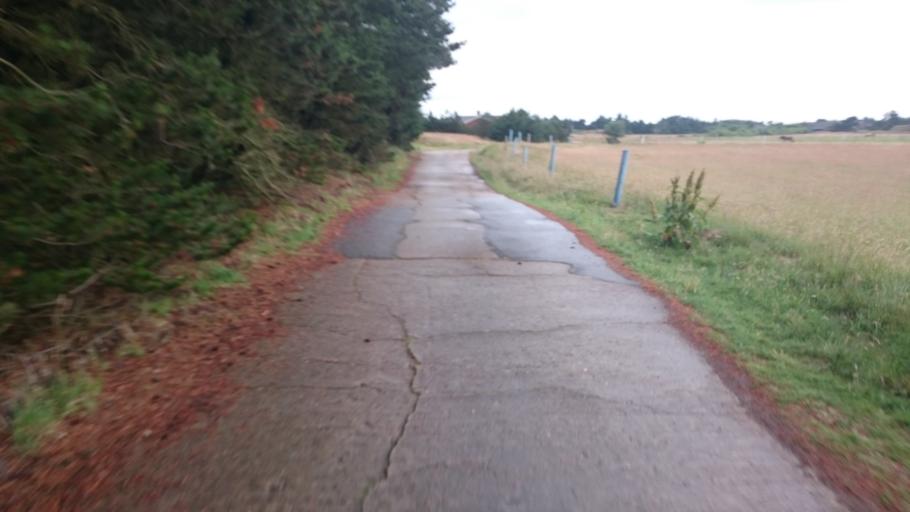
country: DK
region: South Denmark
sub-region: Fano Kommune
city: Nordby
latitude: 55.4329
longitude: 8.3878
